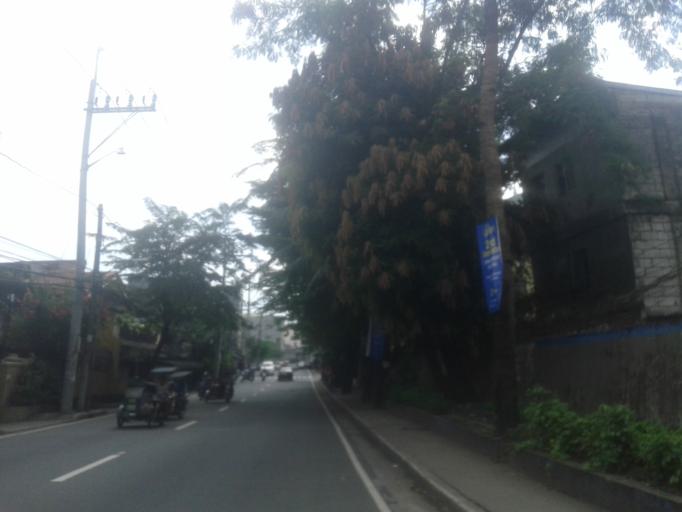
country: PH
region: Metro Manila
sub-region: Mandaluyong
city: Mandaluyong City
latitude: 14.5842
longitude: 121.0448
